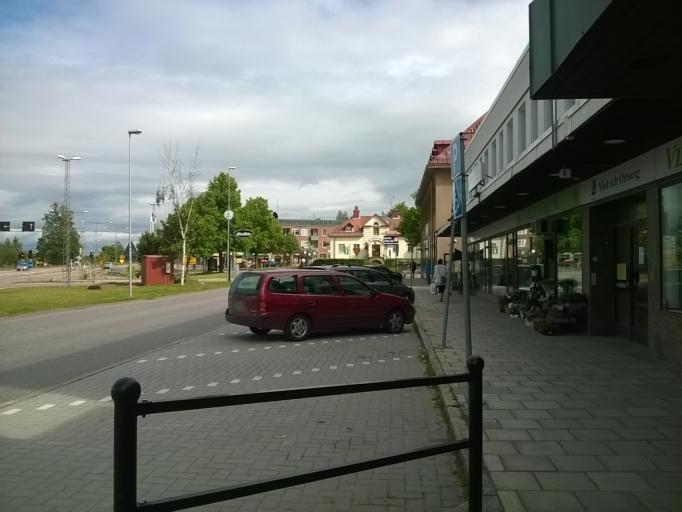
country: SE
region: Dalarna
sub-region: Saters Kommun
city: Saeter
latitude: 60.3476
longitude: 15.7509
